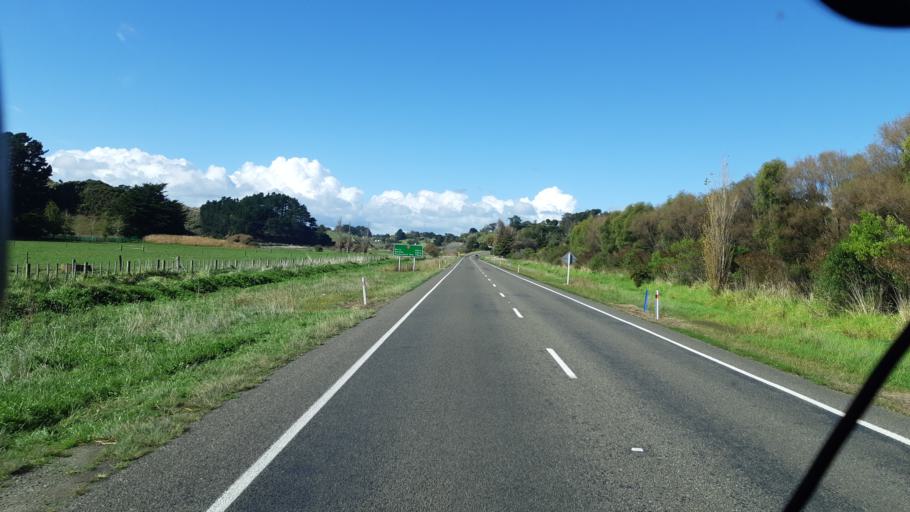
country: NZ
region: Manawatu-Wanganui
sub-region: Wanganui District
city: Wanganui
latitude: -39.9521
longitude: 175.0593
